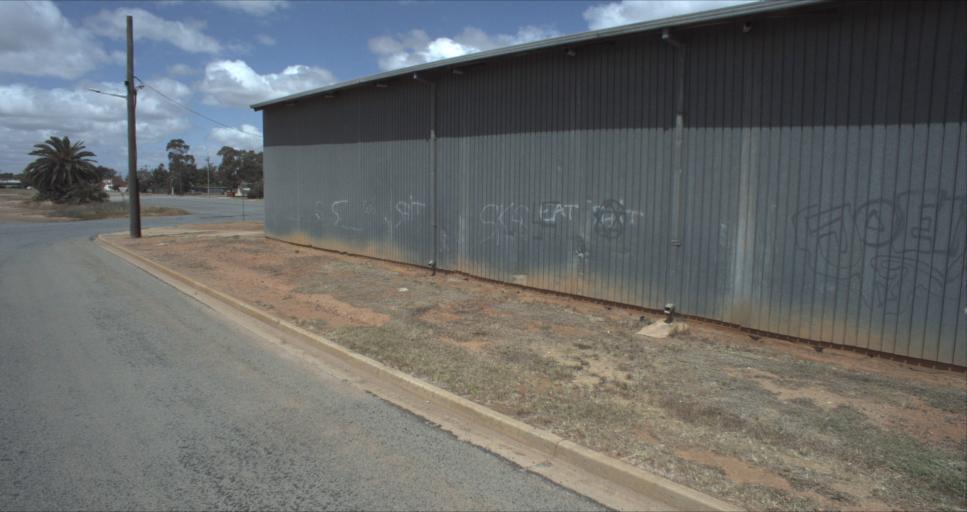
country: AU
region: New South Wales
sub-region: Leeton
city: Leeton
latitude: -34.5537
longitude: 146.3950
